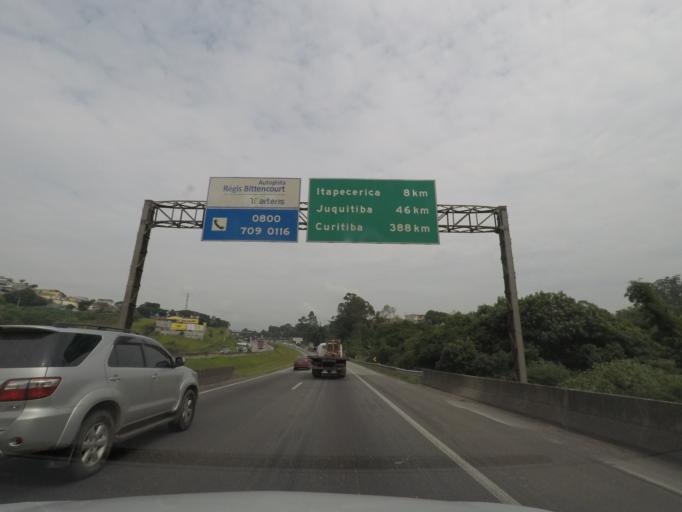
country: BR
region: Sao Paulo
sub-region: Embu
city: Embu
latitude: -23.6502
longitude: -46.8460
